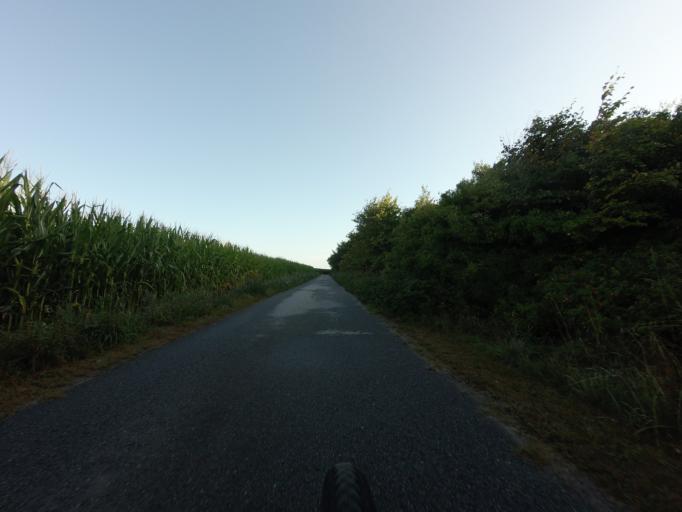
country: DK
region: North Denmark
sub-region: Hjorring Kommune
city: Vra
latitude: 57.3654
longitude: 9.8650
